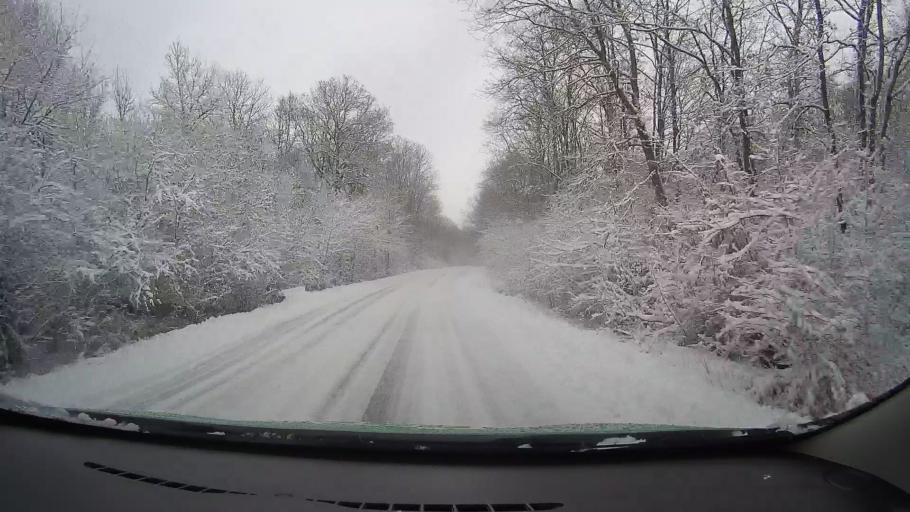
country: RO
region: Hunedoara
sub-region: Comuna Pestisu Mic
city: Pestisu Mic
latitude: 45.8125
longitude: 22.9007
